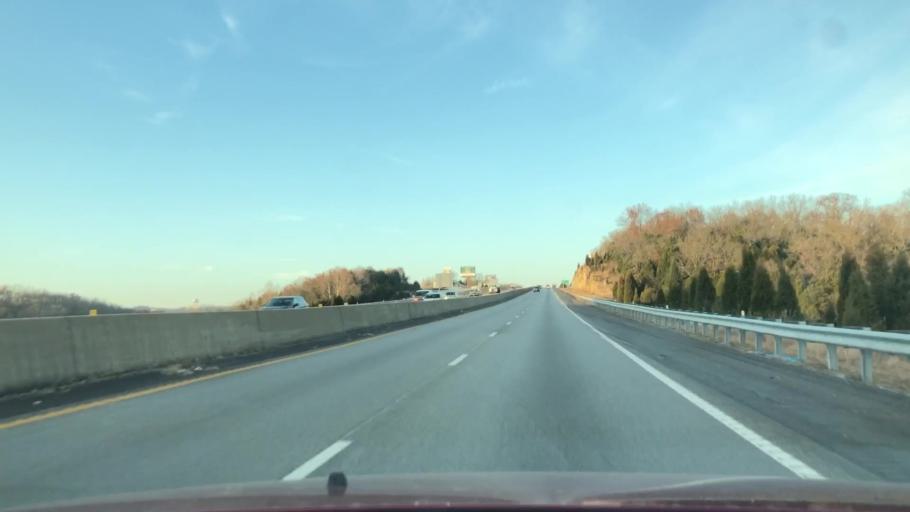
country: US
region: Missouri
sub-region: Taney County
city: Branson
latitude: 36.6750
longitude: -93.2211
